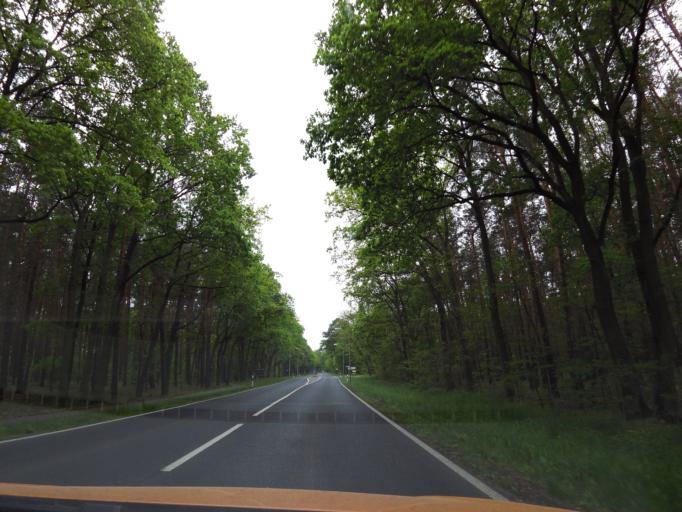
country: DE
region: Brandenburg
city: Beelitz
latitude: 52.2034
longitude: 12.9581
